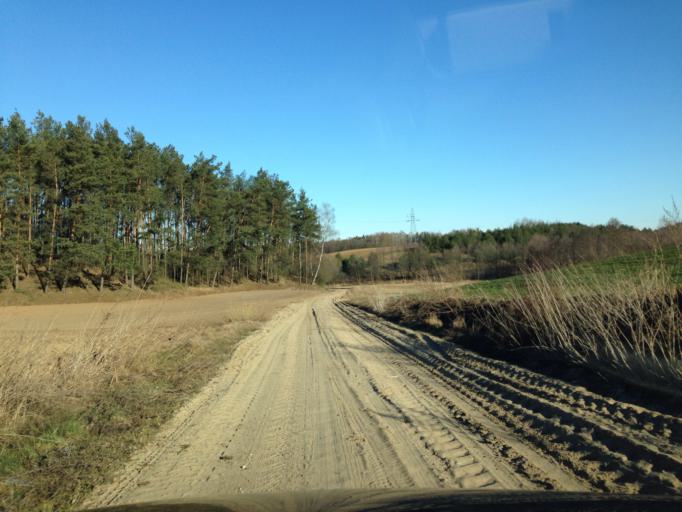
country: PL
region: Kujawsko-Pomorskie
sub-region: Powiat brodnicki
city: Brzozie
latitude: 53.3013
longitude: 19.6566
